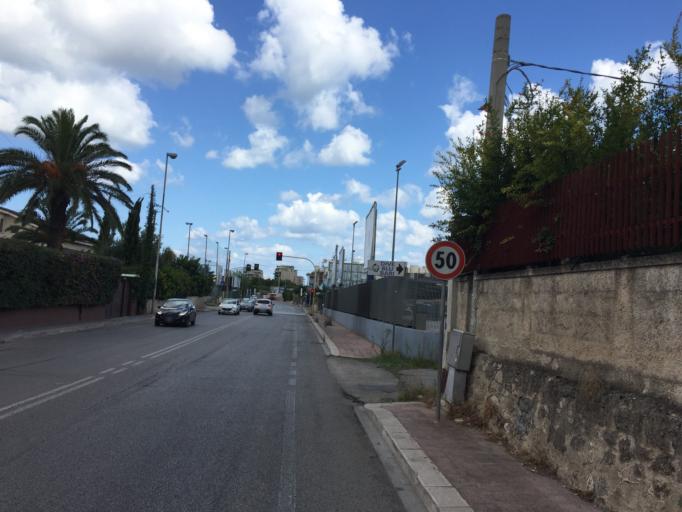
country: IT
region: Apulia
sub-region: Provincia di Bari
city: Bari
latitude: 41.0896
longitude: 16.8837
